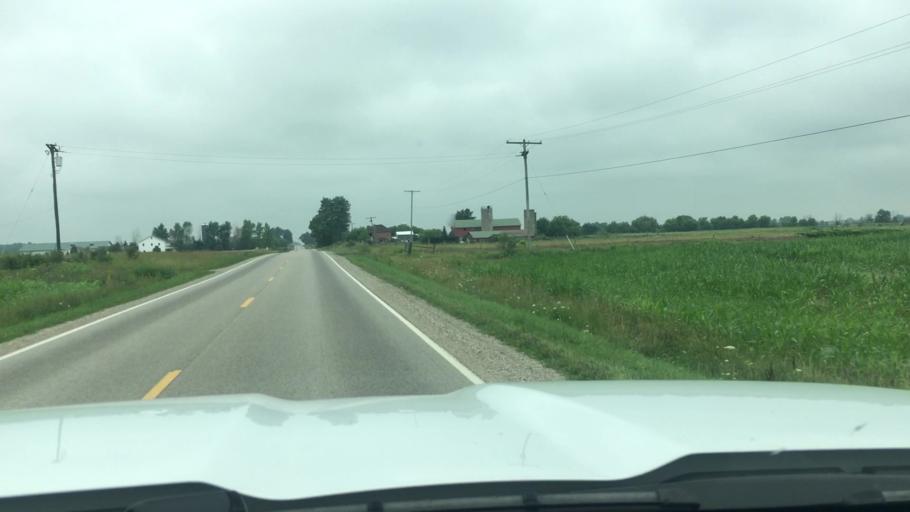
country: US
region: Michigan
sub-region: Sanilac County
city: Brown City
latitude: 43.2684
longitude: -82.9822
